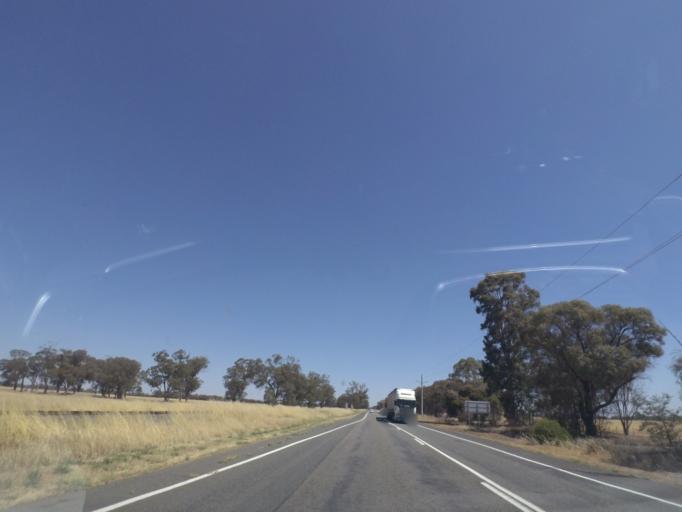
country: AU
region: Victoria
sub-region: Greater Shepparton
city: Shepparton
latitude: -36.2000
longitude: 145.4318
